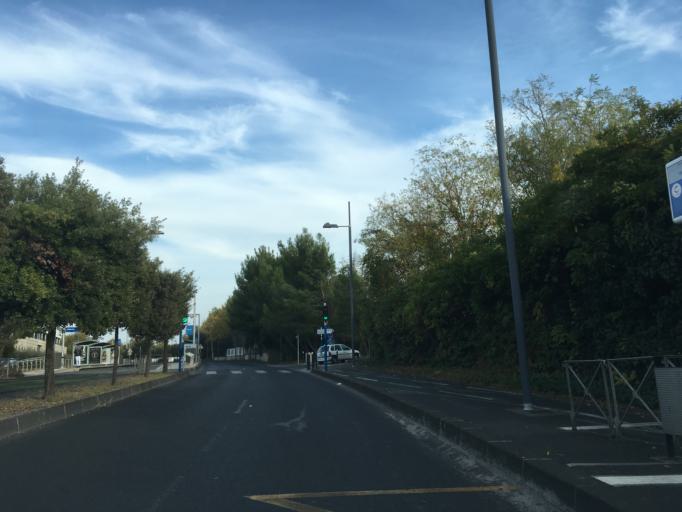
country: FR
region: Languedoc-Roussillon
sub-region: Departement de l'Herault
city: Castelnau-le-Lez
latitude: 43.6032
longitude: 3.9091
